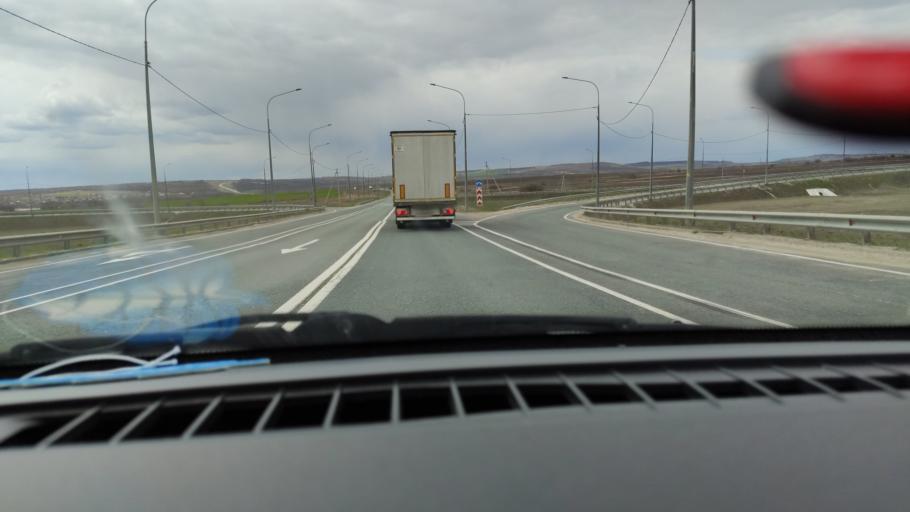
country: RU
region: Saratov
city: Yelshanka
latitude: 51.8305
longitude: 46.4147
